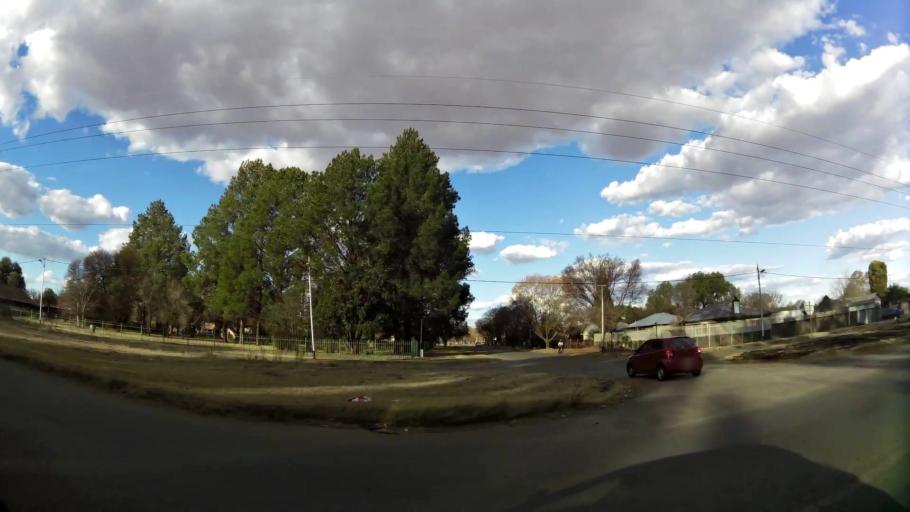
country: ZA
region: North-West
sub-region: Dr Kenneth Kaunda District Municipality
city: Potchefstroom
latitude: -26.7014
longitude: 27.0785
